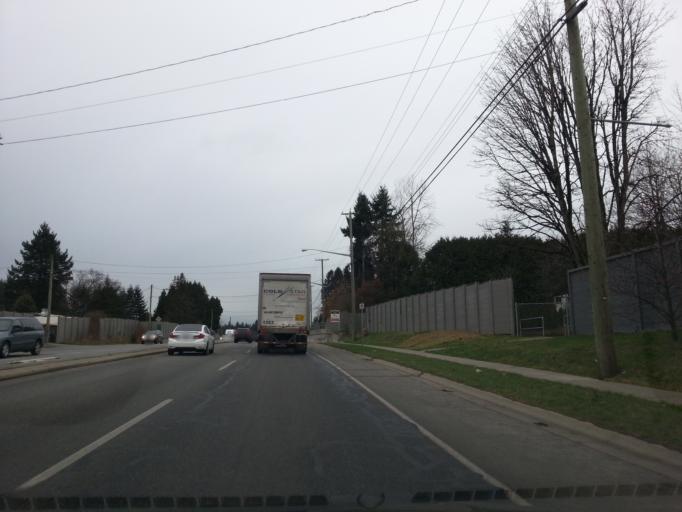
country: CA
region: British Columbia
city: Surrey
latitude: 49.1046
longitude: -122.8141
